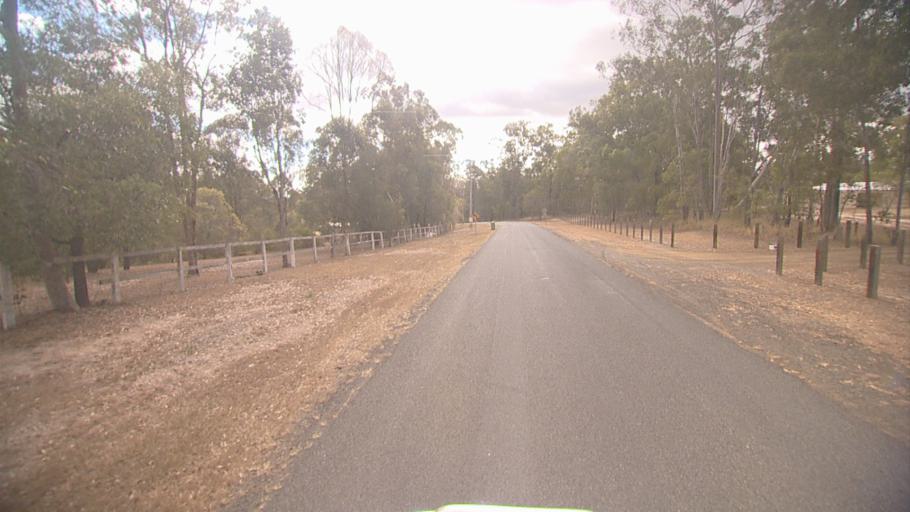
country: AU
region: Queensland
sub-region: Logan
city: Cedar Vale
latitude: -27.8768
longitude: 153.0273
